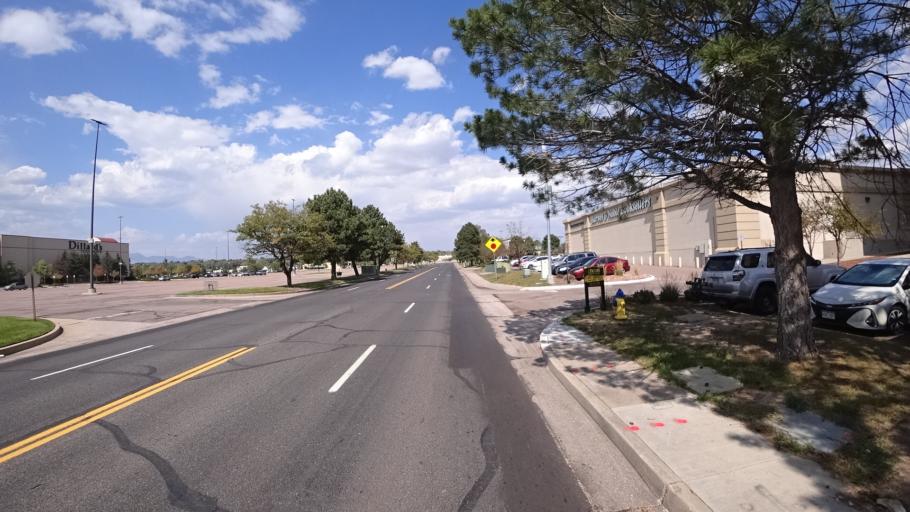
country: US
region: Colorado
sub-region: El Paso County
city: Cimarron Hills
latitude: 38.8430
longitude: -104.7587
